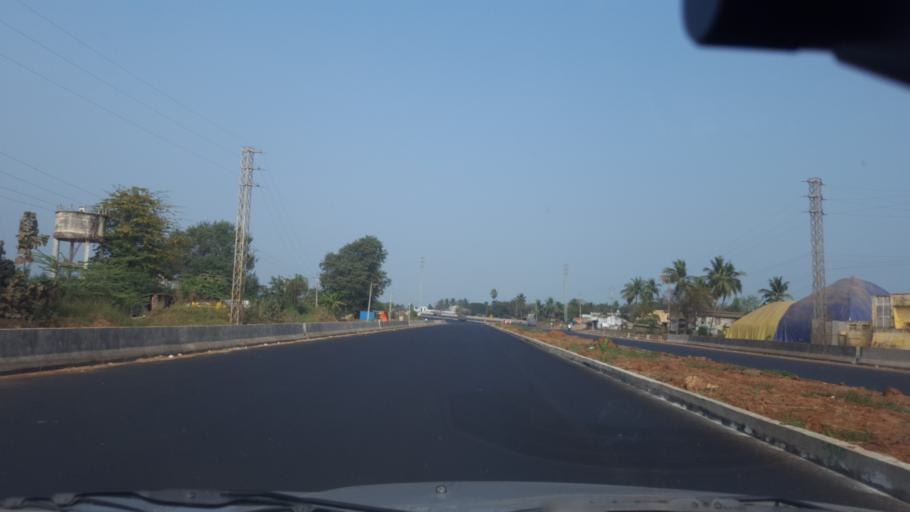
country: IN
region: Andhra Pradesh
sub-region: West Godavari
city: Eluru
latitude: 16.6490
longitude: 80.9947
